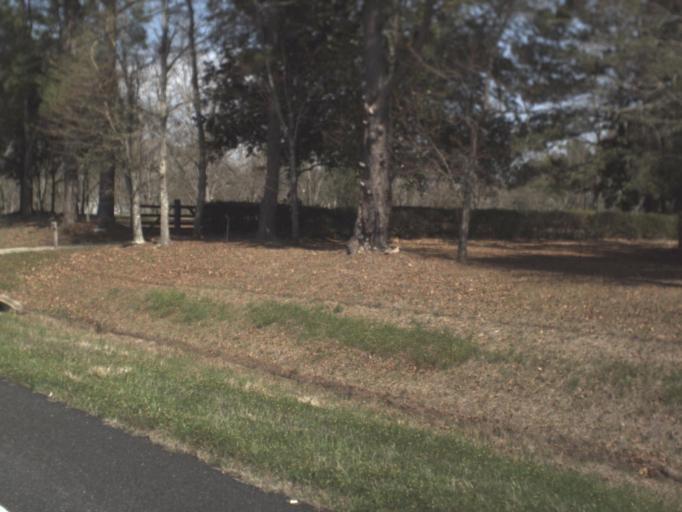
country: US
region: Florida
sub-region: Gadsden County
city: Havana
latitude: 30.5916
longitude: -84.4074
